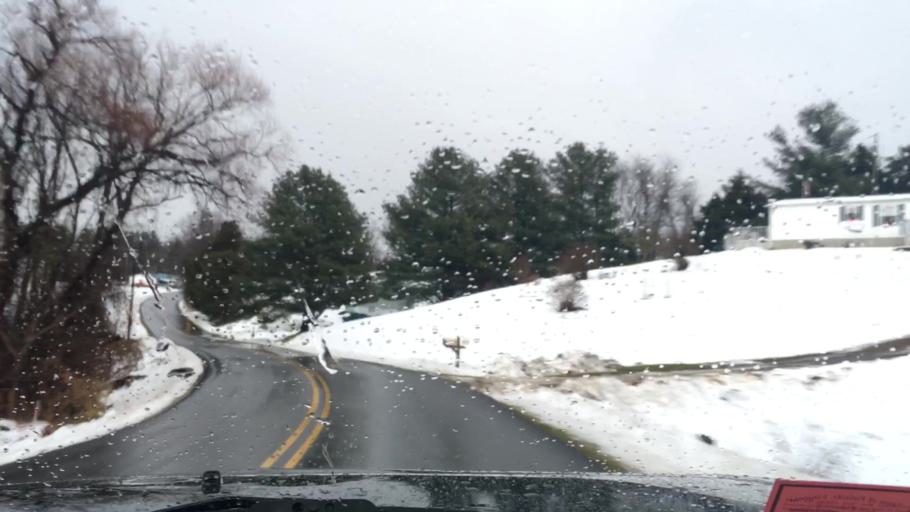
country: US
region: Virginia
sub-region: Pulaski County
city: Dublin
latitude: 37.0137
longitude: -80.6480
